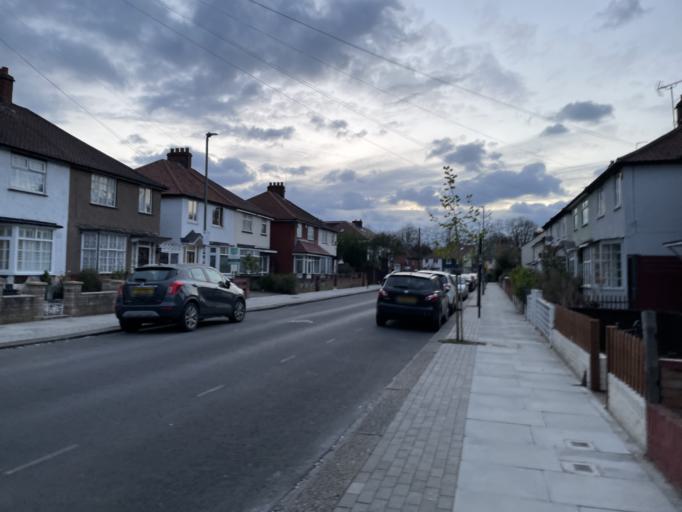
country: GB
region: England
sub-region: Greater London
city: Earlsfield
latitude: 51.4317
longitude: -0.1727
